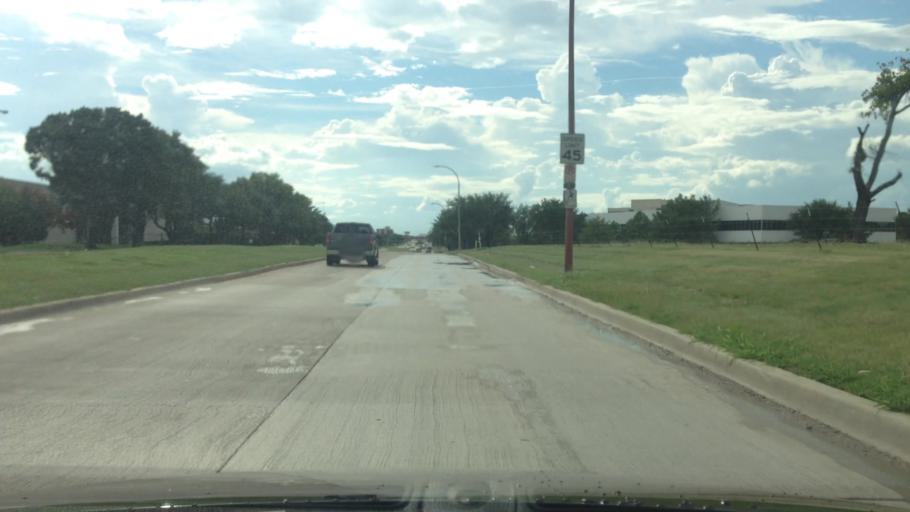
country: US
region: Texas
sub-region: Tarrant County
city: Haltom City
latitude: 32.8244
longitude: -97.3005
